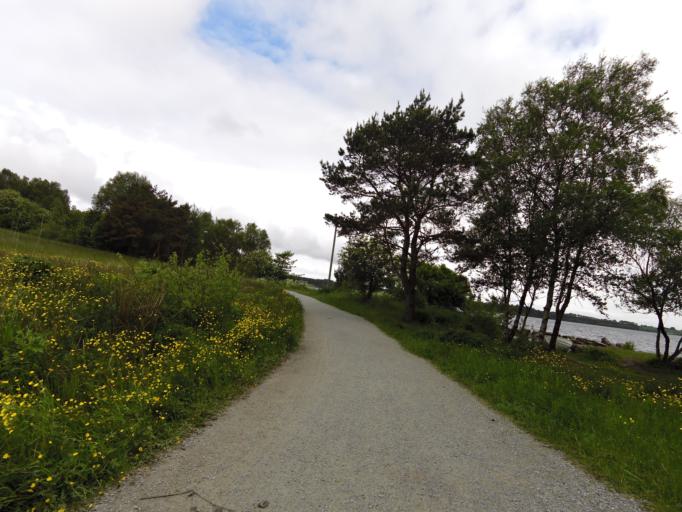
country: NO
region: Rogaland
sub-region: Stavanger
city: Stavanger
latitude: 58.9587
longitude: 5.6741
